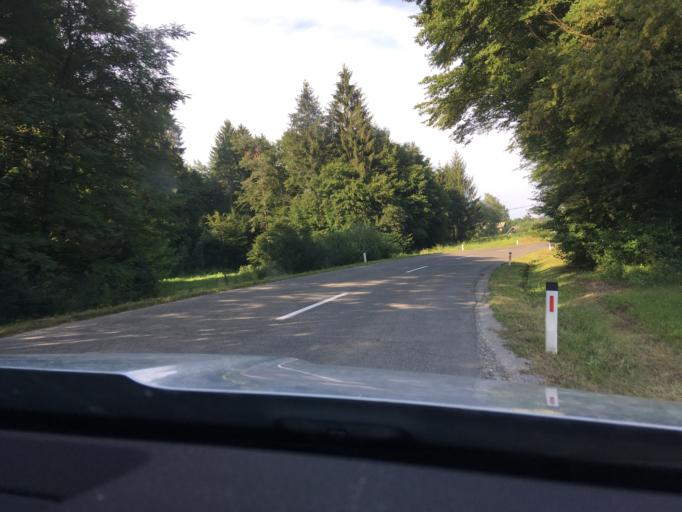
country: SI
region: Metlika
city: Metlika
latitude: 45.6149
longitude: 15.2719
